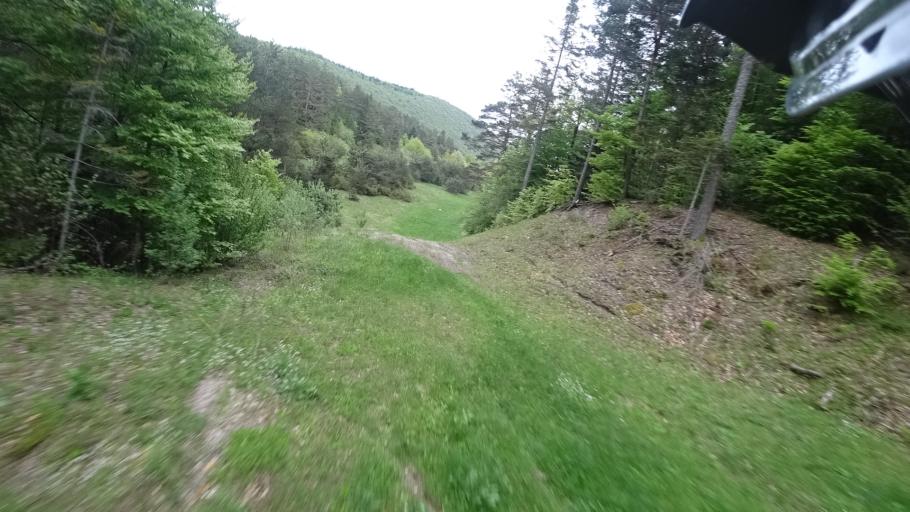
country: HR
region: Licko-Senjska
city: Jezerce
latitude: 44.8790
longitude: 15.4343
